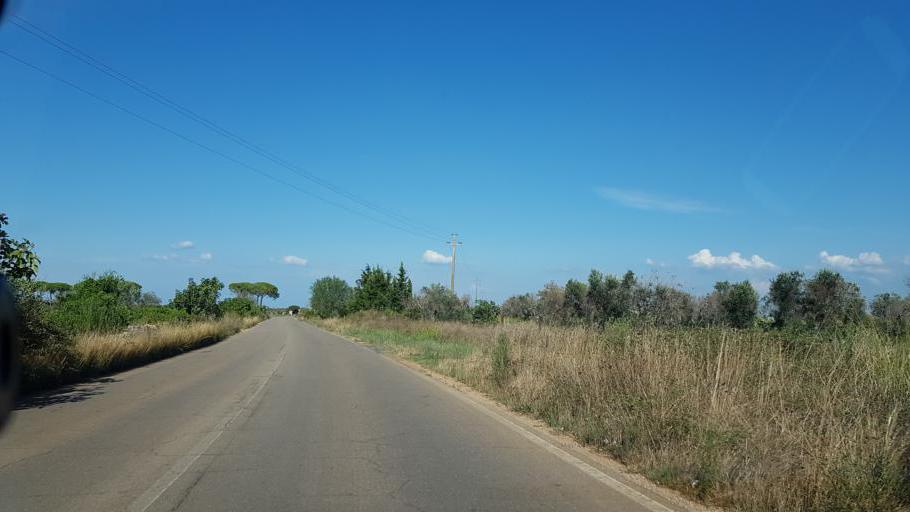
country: IT
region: Apulia
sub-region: Provincia di Lecce
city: Monteroni di Lecce
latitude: 40.2876
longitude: 18.0815
